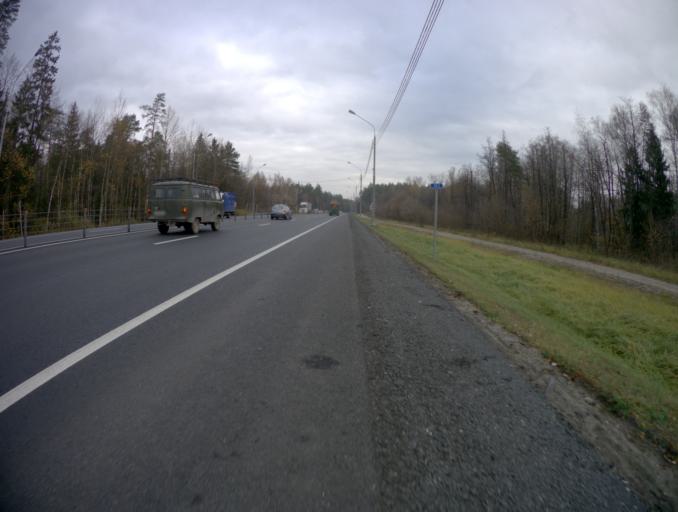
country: RU
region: Moskovskaya
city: Malaya Dubna
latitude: 55.8601
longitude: 38.9626
